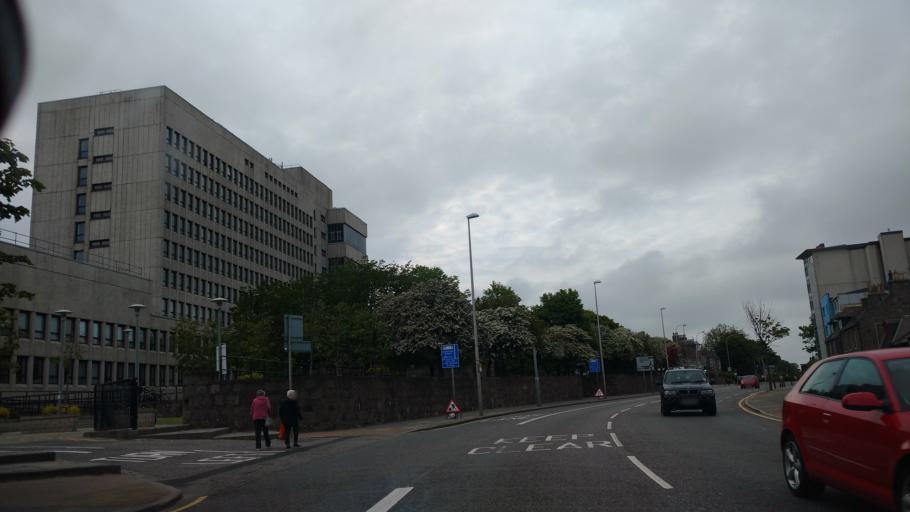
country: GB
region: Scotland
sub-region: Aberdeen City
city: Aberdeen
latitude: 57.1652
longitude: -2.0975
